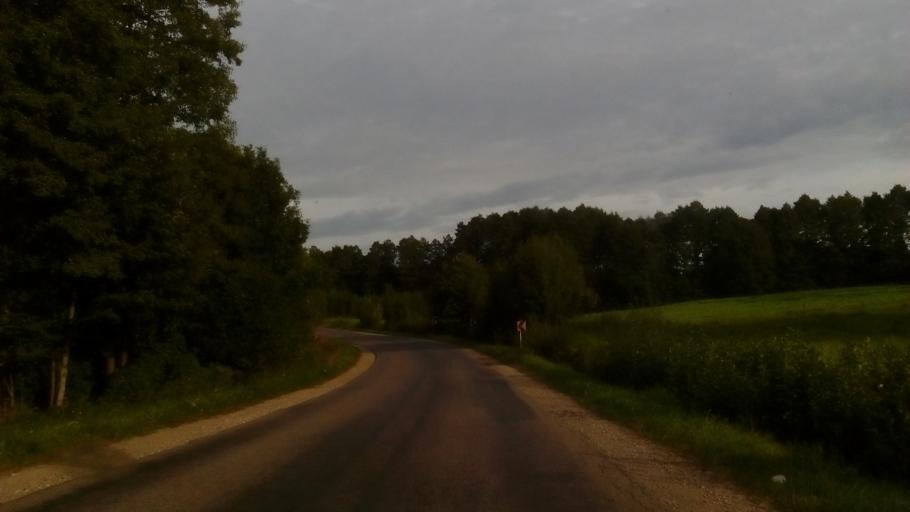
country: LT
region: Alytaus apskritis
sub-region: Alytus
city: Alytus
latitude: 54.3282
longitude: 23.9189
